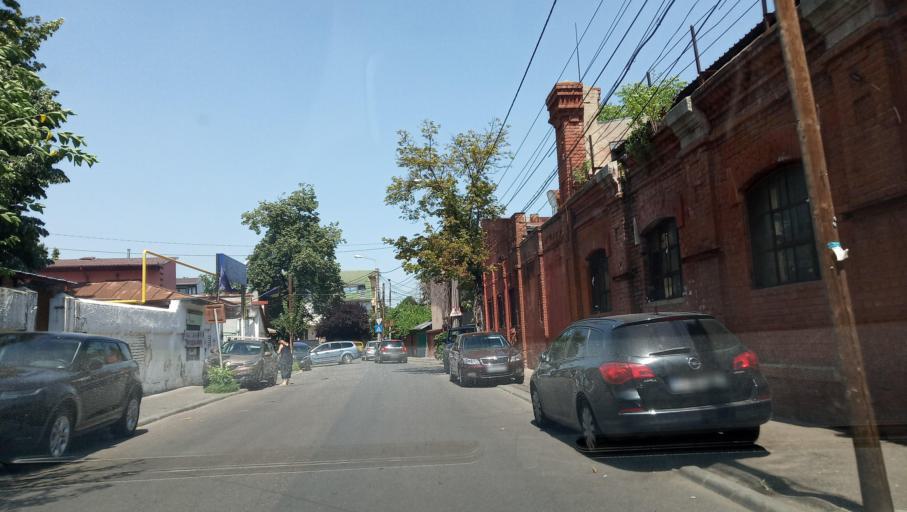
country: RO
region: Bucuresti
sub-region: Municipiul Bucuresti
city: Bucharest
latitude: 44.4553
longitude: 26.1157
